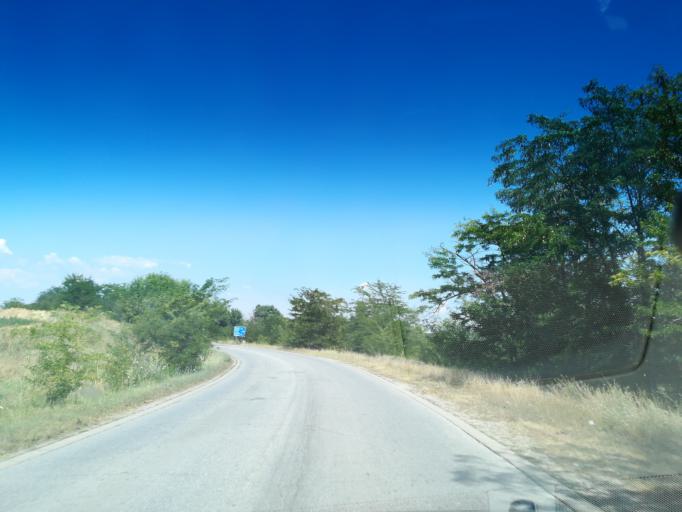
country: BG
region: Plovdiv
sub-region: Obshtina Sadovo
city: Sadovo
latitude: 42.0399
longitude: 25.1332
